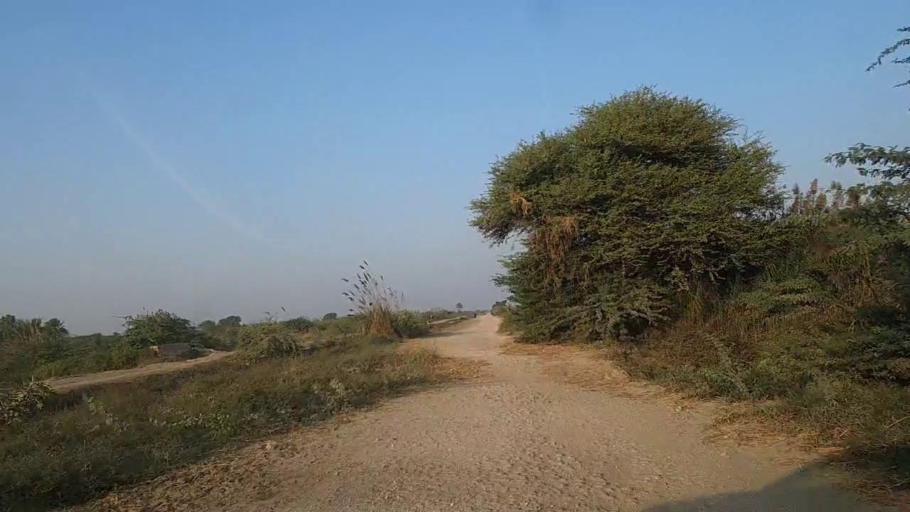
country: PK
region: Sindh
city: Keti Bandar
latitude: 24.2743
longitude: 67.6827
